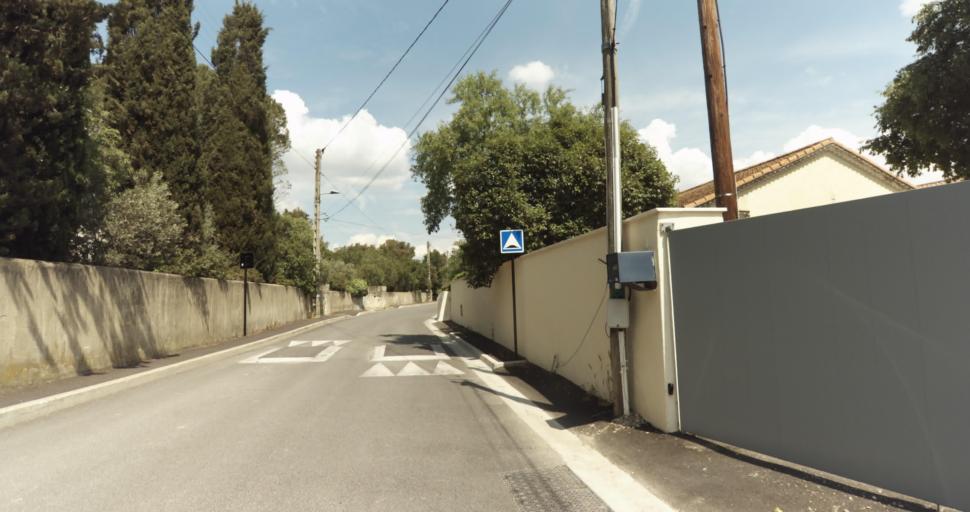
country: FR
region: Languedoc-Roussillon
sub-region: Departement du Gard
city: Nimes
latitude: 43.8578
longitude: 4.3482
